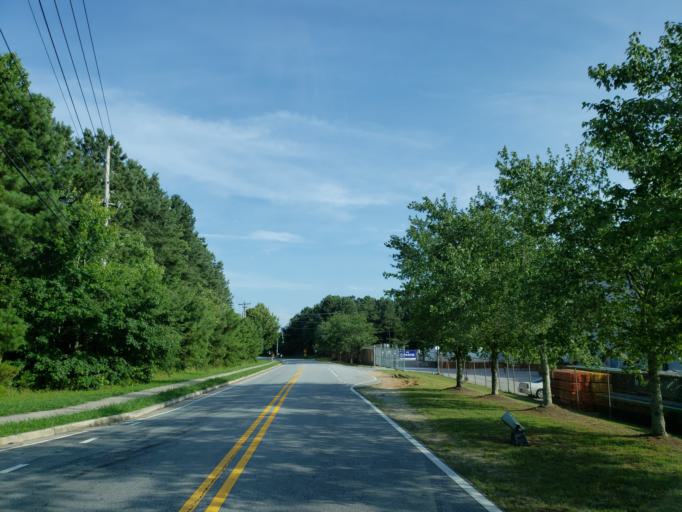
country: US
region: Georgia
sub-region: Cobb County
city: Powder Springs
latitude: 33.8725
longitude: -84.7027
